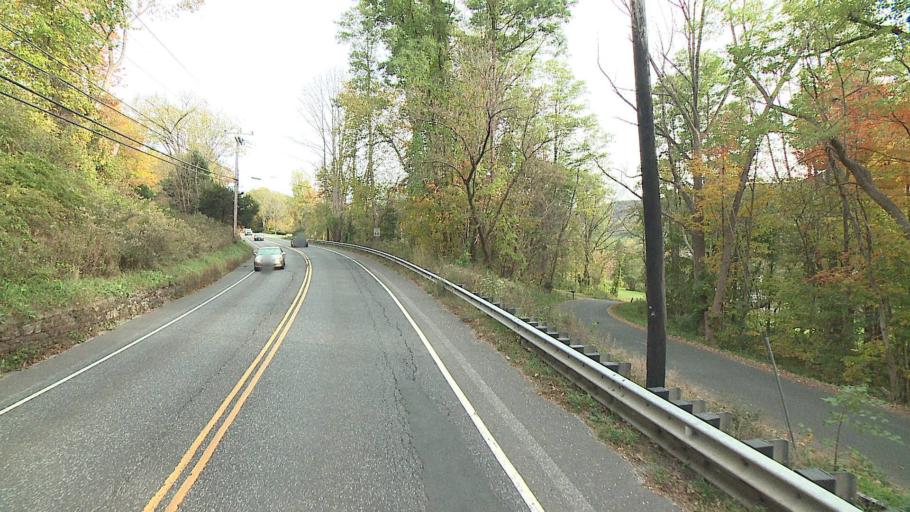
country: US
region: Connecticut
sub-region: Litchfield County
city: Canaan
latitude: 42.0185
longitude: -73.3107
